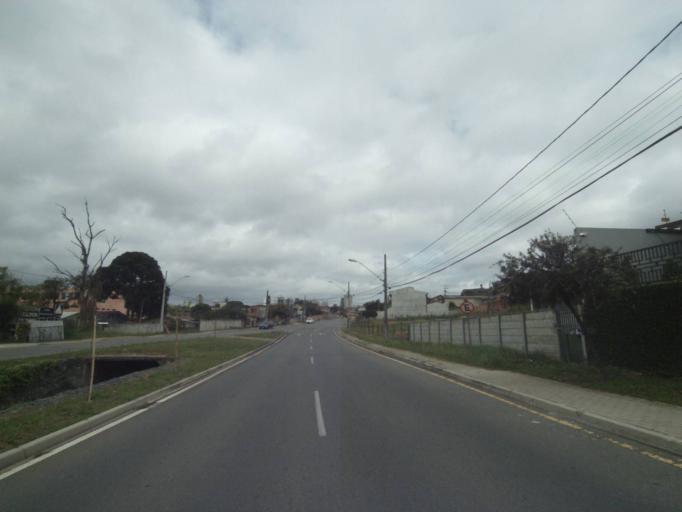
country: BR
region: Parana
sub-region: Pinhais
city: Pinhais
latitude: -25.4347
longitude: -49.2254
